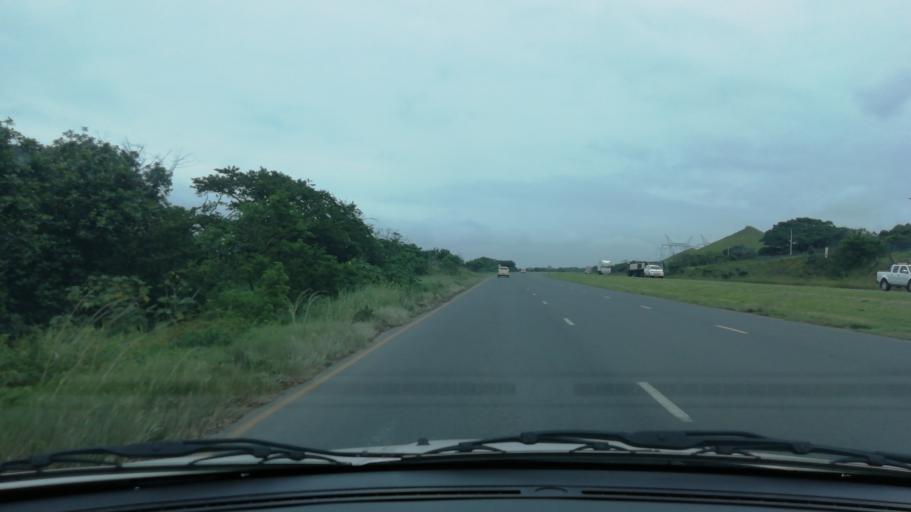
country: ZA
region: KwaZulu-Natal
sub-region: uThungulu District Municipality
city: Richards Bay
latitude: -28.7714
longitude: 32.0299
